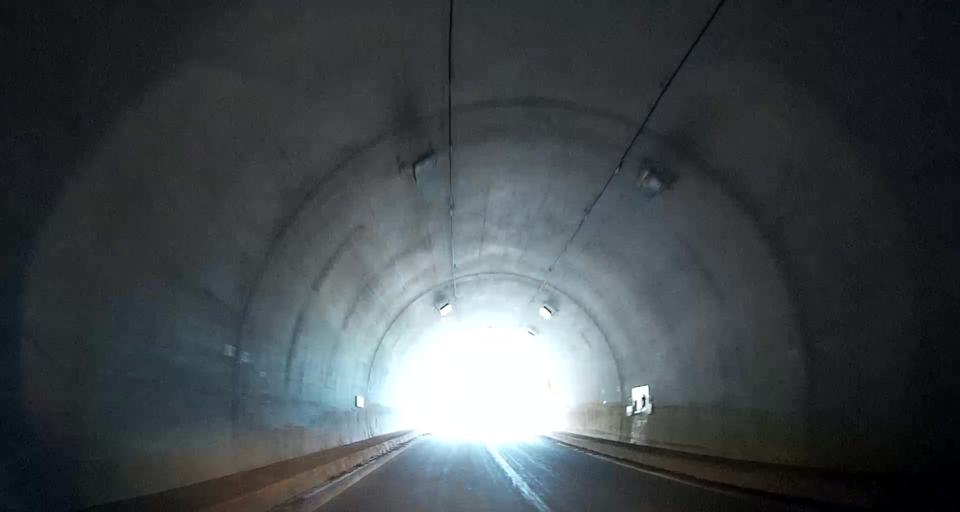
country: JP
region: Hokkaido
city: Chitose
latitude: 42.7906
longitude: 142.0419
